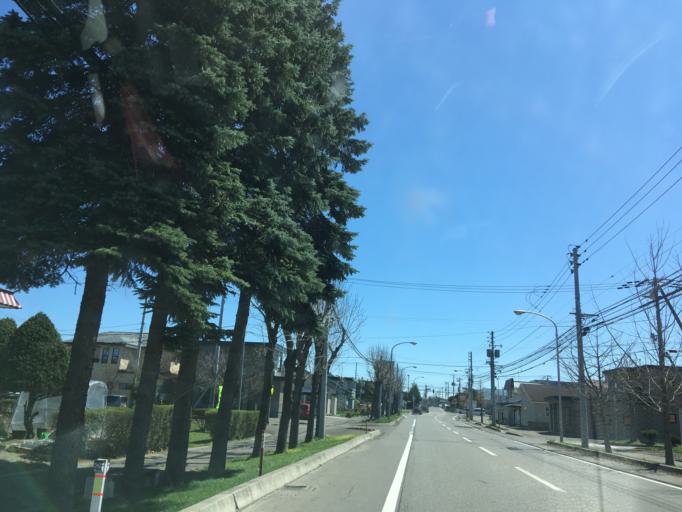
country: JP
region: Hokkaido
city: Obihiro
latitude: 42.9212
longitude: 143.1714
